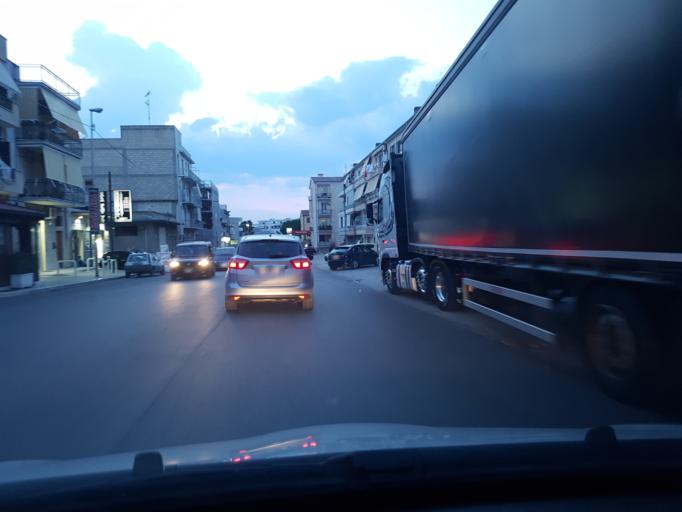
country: IT
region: Apulia
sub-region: Provincia di Foggia
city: Cerignola
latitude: 41.2610
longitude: 15.8909
